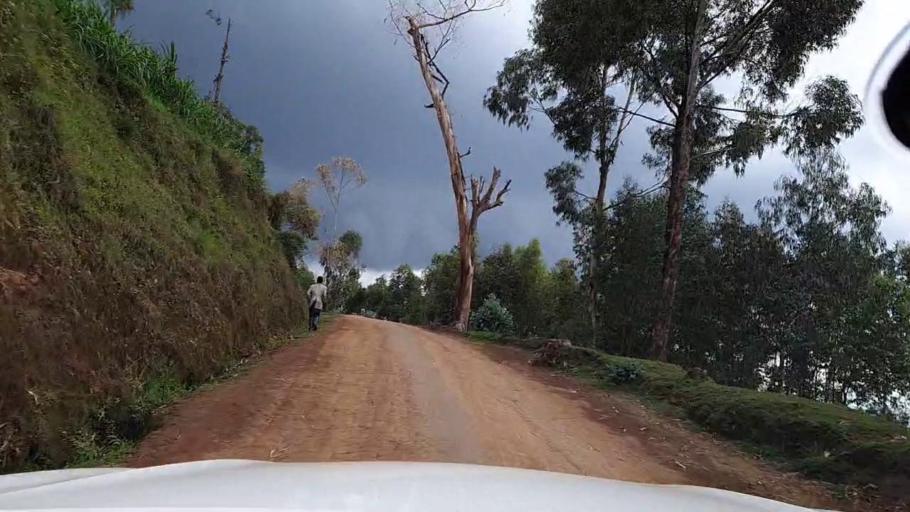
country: BI
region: Kayanza
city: Kayanza
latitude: -2.7915
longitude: 29.5217
